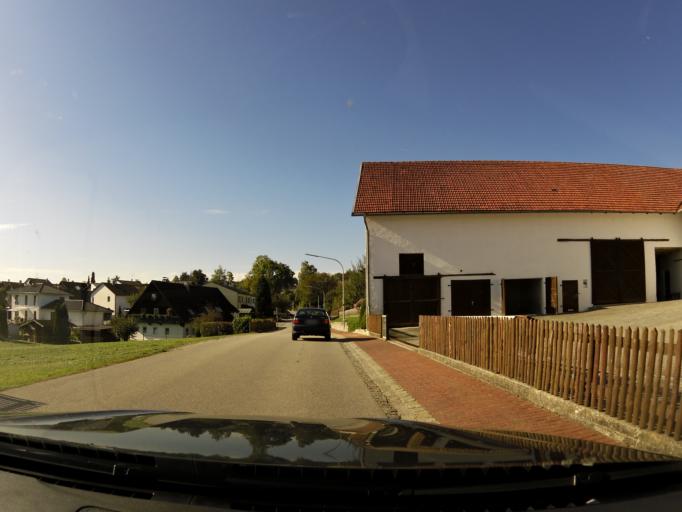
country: DE
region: Bavaria
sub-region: Lower Bavaria
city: Tiefenbach
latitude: 48.4876
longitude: 12.0972
